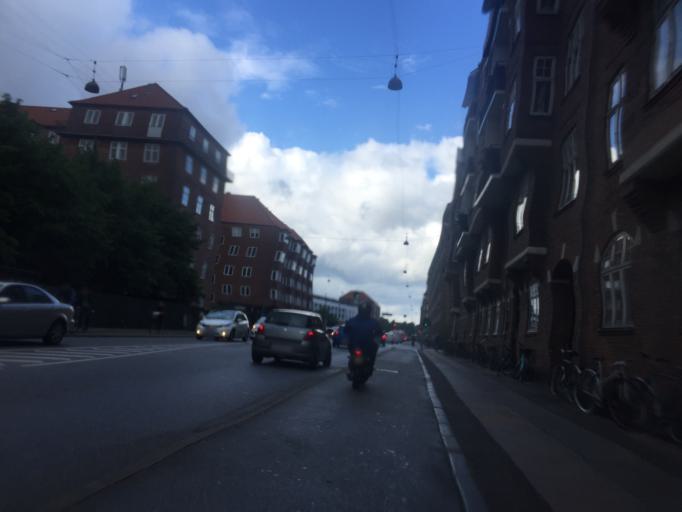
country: DK
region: Capital Region
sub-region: Kobenhavn
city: Christianshavn
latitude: 55.6648
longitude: 12.5947
